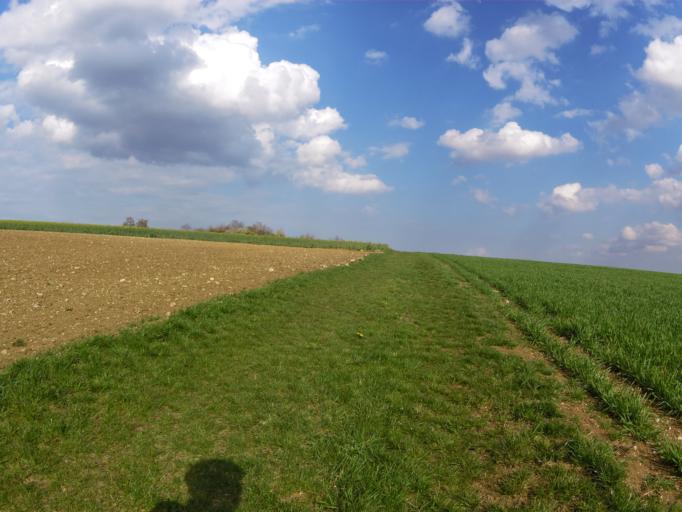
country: DE
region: Bavaria
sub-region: Regierungsbezirk Unterfranken
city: Rimpar
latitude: 49.8647
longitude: 9.9470
